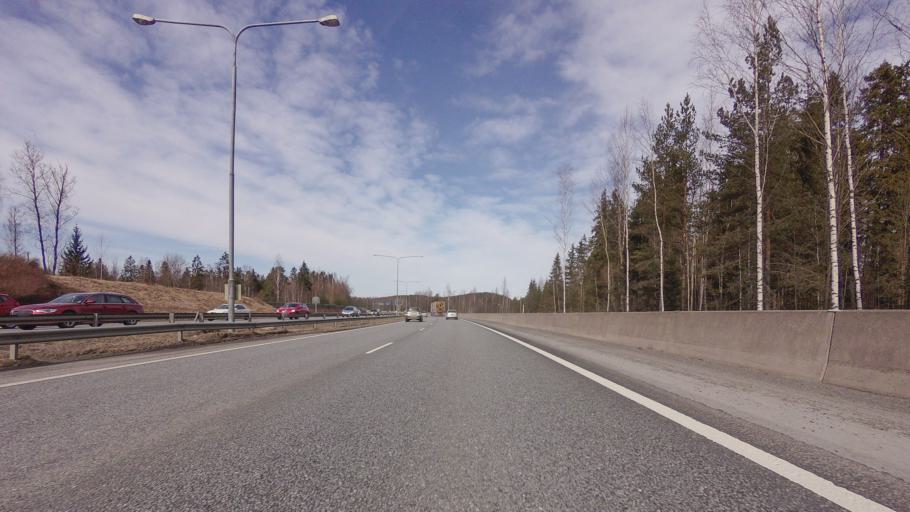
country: FI
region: Pirkanmaa
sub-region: Tampere
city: Tampere
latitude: 61.4149
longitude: 23.7649
